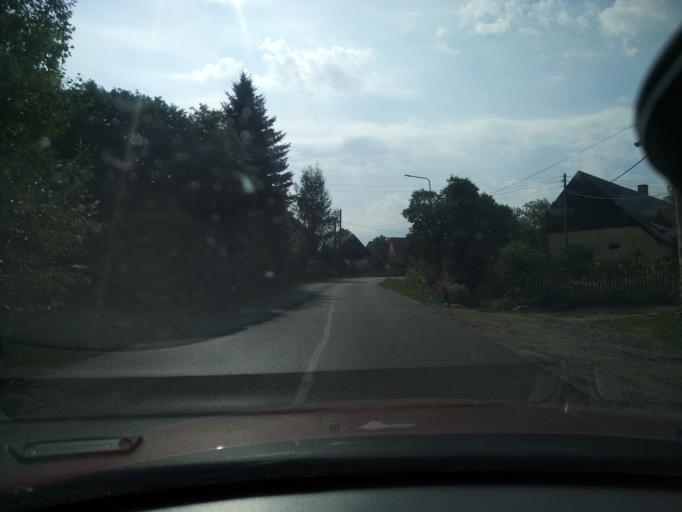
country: PL
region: Lower Silesian Voivodeship
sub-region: Powiat jeleniogorski
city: Stara Kamienica
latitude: 50.9012
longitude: 15.5721
